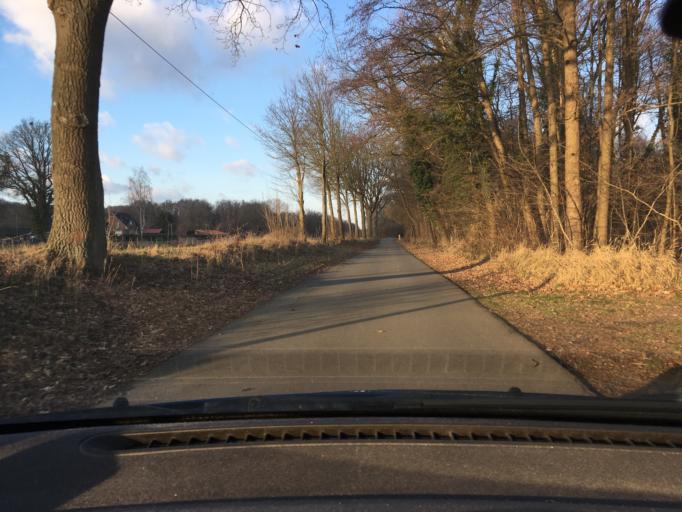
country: DE
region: Schleswig-Holstein
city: Witzeeze
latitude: 53.4569
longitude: 10.6257
